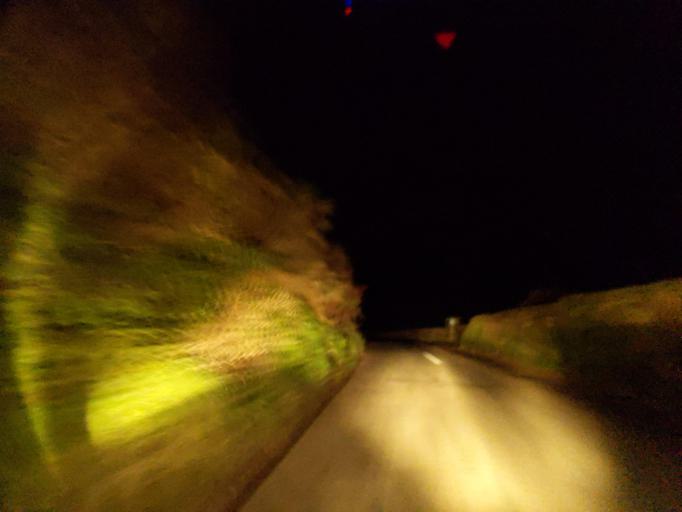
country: GB
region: England
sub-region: Cornwall
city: Saltash
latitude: 50.3623
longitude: -4.2899
